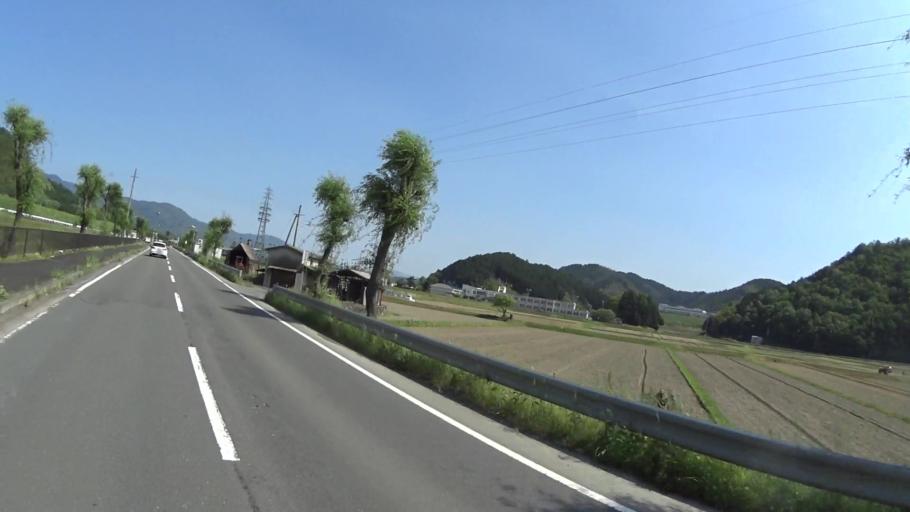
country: JP
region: Kyoto
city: Kameoka
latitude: 35.1083
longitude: 135.5218
